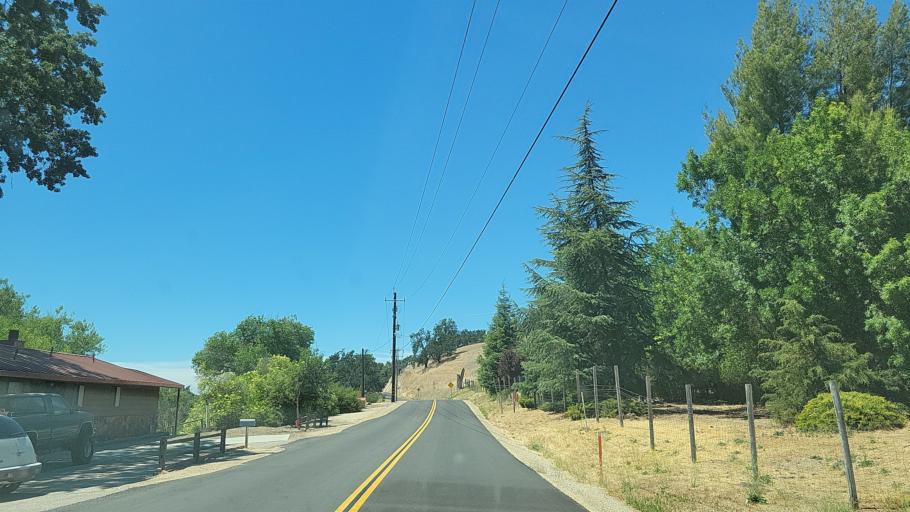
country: US
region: California
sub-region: San Luis Obispo County
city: Atascadero
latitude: 35.4882
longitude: -120.6377
